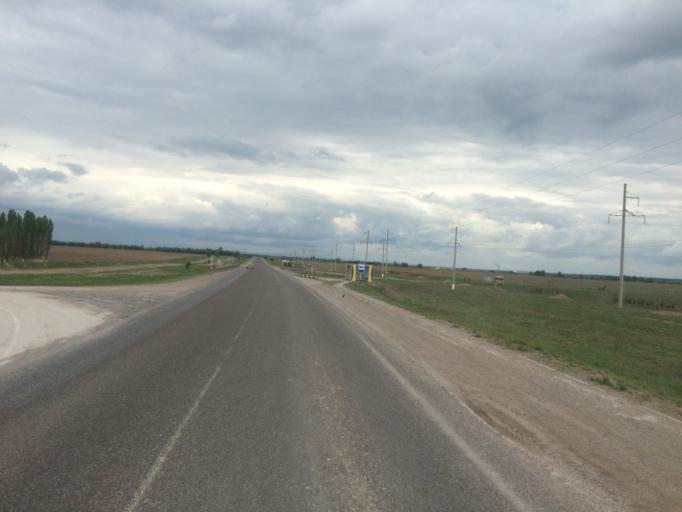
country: KG
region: Chuy
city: Sokuluk
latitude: 43.2463
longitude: 74.3009
